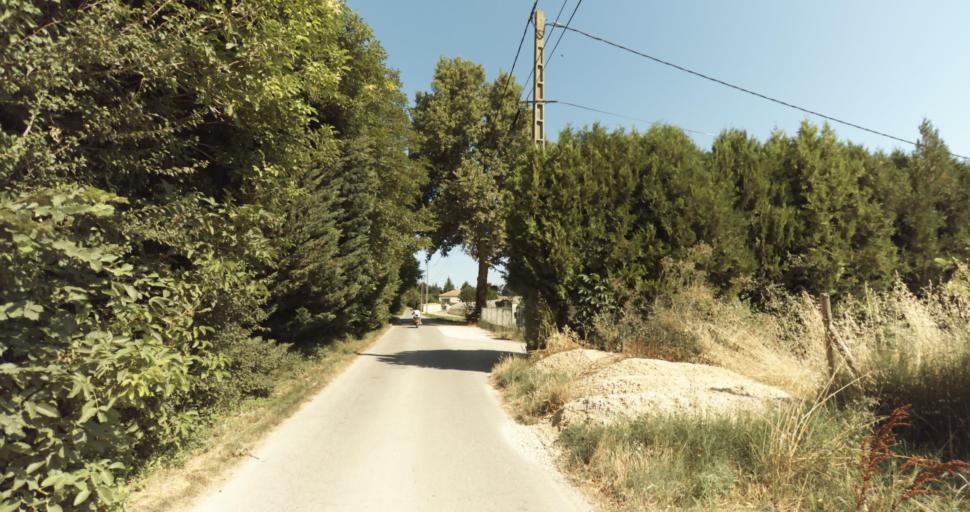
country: FR
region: Provence-Alpes-Cote d'Azur
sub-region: Departement du Vaucluse
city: Althen-des-Paluds
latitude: 44.0106
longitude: 4.9810
